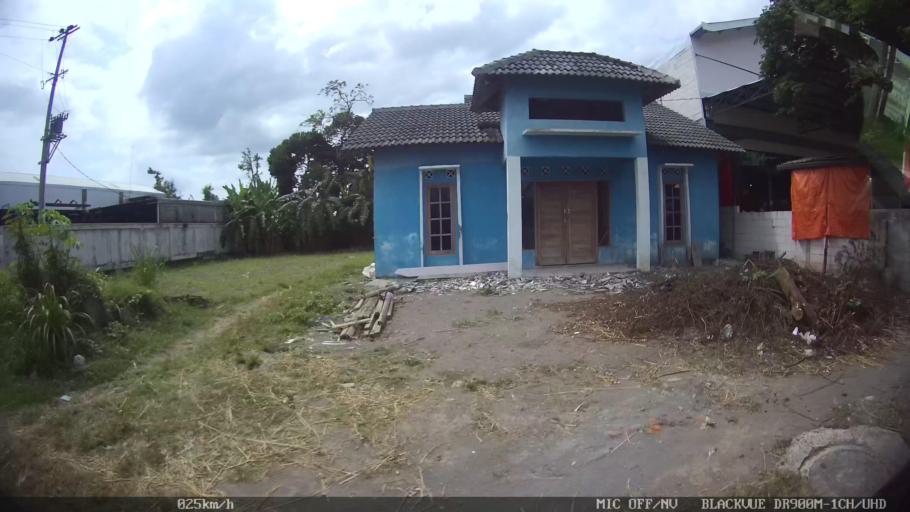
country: ID
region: Daerah Istimewa Yogyakarta
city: Depok
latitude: -7.8118
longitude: 110.4431
